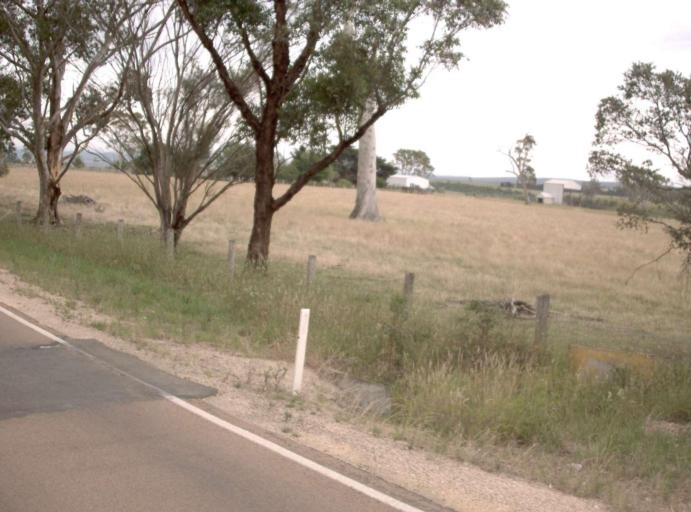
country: AU
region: Victoria
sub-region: East Gippsland
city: Bairnsdale
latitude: -37.8296
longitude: 147.5437
